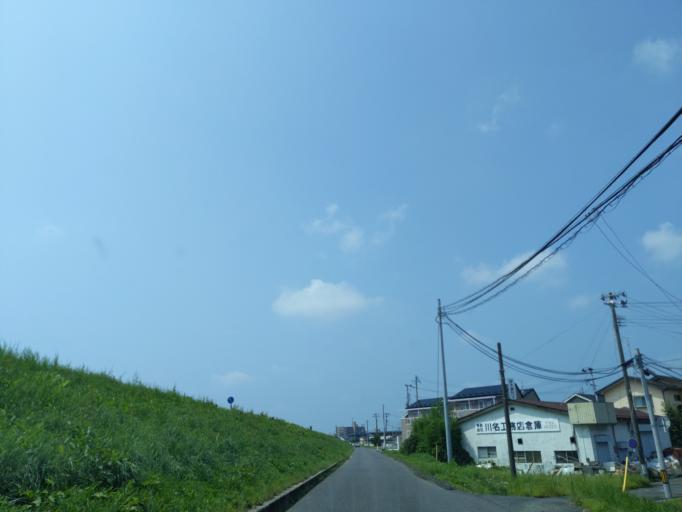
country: JP
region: Fukushima
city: Koriyama
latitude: 37.3854
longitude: 140.3967
